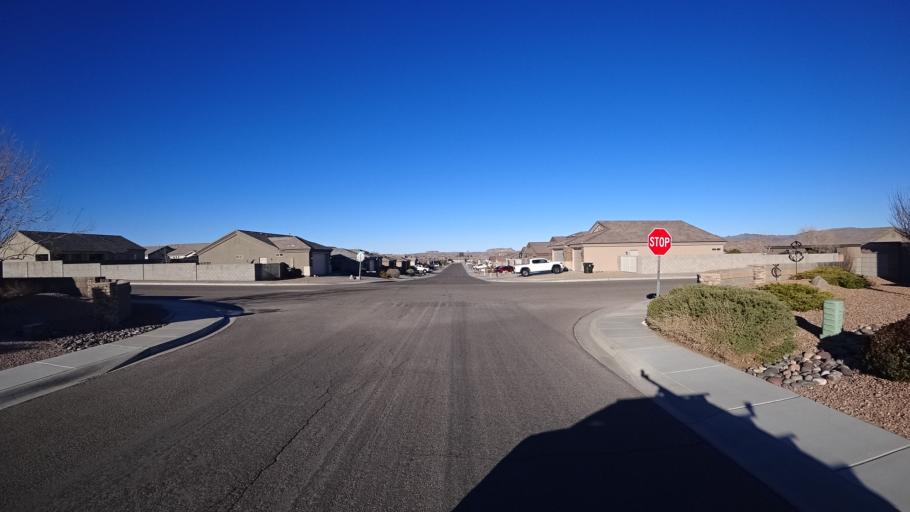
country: US
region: Arizona
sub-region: Mohave County
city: Kingman
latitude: 35.1929
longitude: -113.9980
